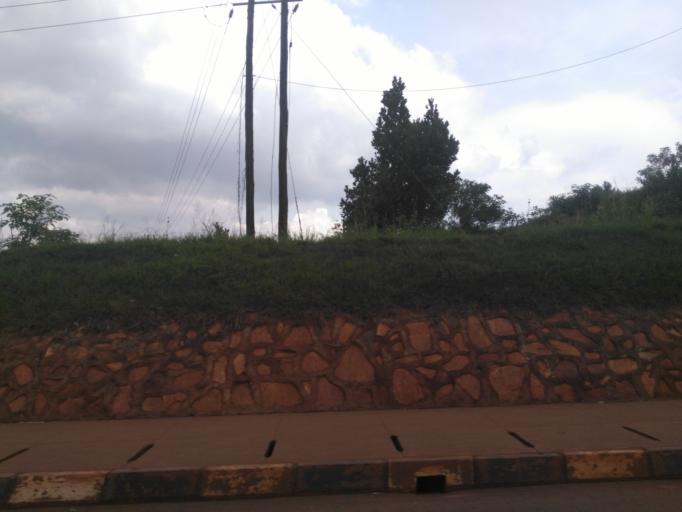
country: UG
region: Eastern Region
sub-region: Jinja District
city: Jinja
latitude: 0.4434
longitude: 33.1988
